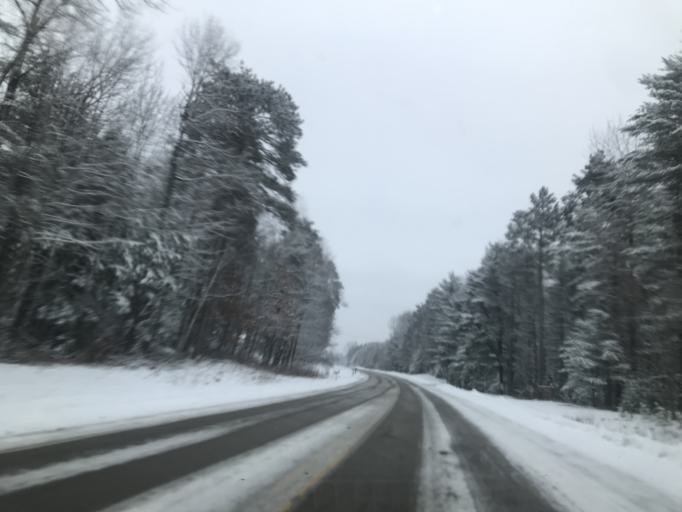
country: US
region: Wisconsin
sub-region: Oconto County
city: Oconto Falls
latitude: 44.8603
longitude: -88.0666
